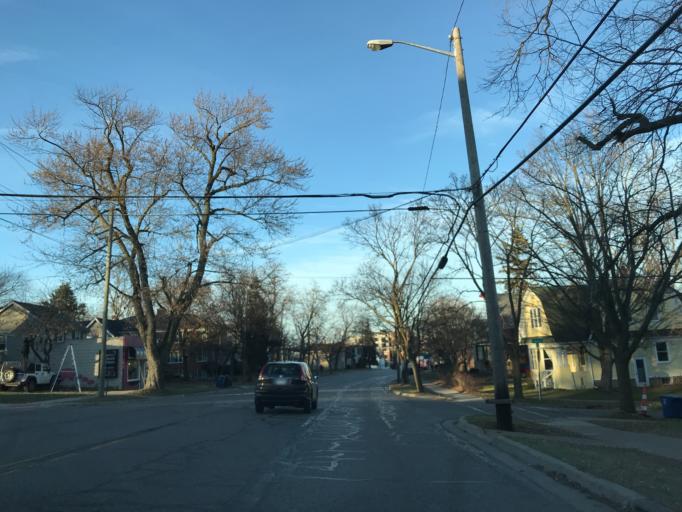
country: US
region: Michigan
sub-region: Washtenaw County
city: Ann Arbor
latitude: 42.2698
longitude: -83.7501
